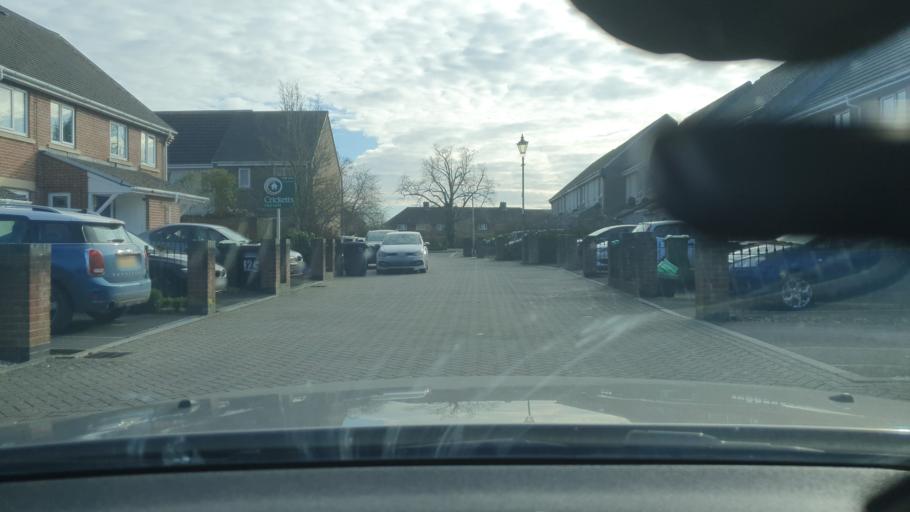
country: GB
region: England
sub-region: West Berkshire
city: Greenham
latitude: 51.3862
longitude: -1.3247
